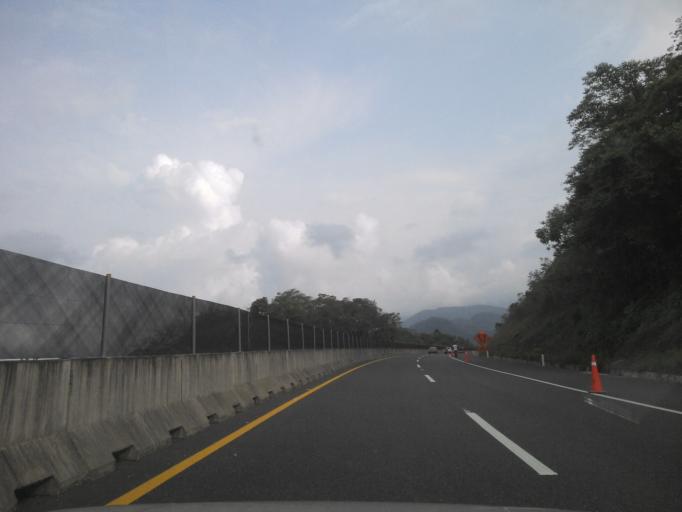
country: MX
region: Puebla
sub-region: Xicotepec
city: San Lorenzo
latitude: 20.3818
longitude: -97.9443
